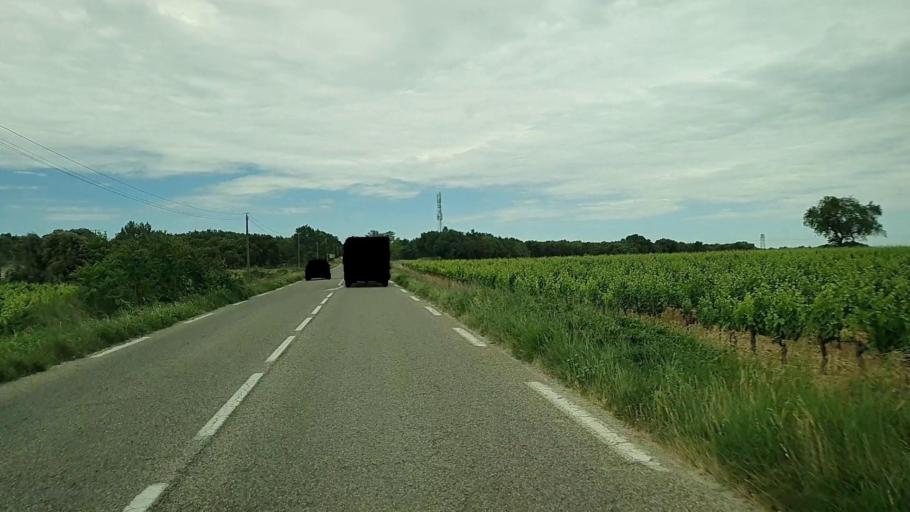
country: FR
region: Languedoc-Roussillon
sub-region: Departement du Gard
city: Connaux
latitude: 44.0490
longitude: 4.5735
